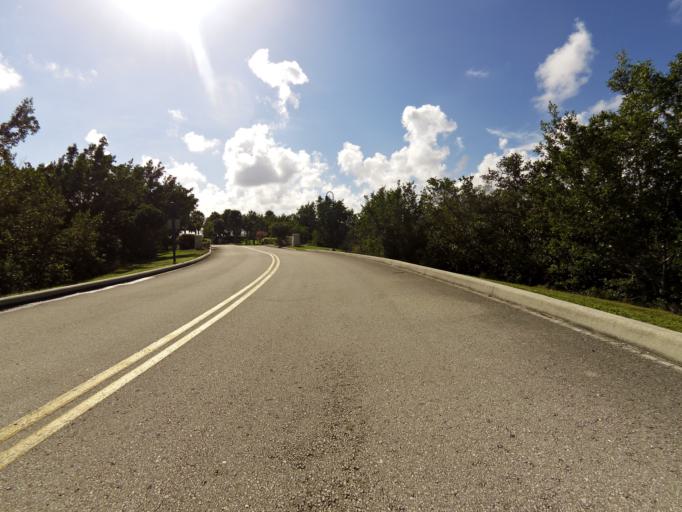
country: US
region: Florida
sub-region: Broward County
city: Dania Beach
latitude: 26.0353
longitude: -80.1203
